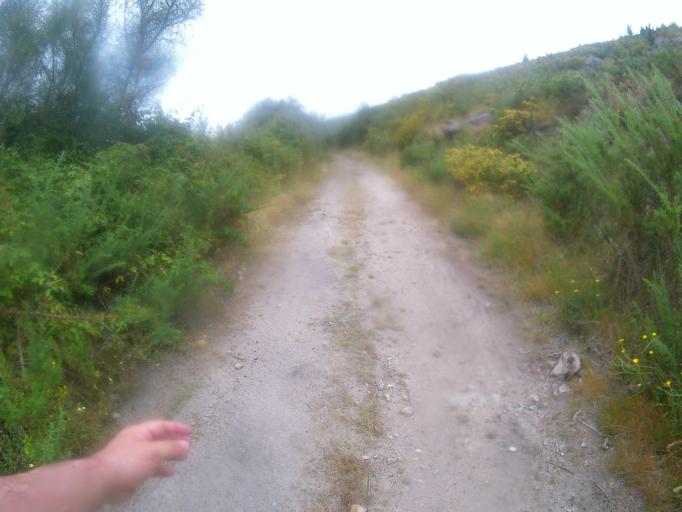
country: PT
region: Viana do Castelo
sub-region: Ponte de Lima
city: Ponte de Lima
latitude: 41.7165
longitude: -8.6030
